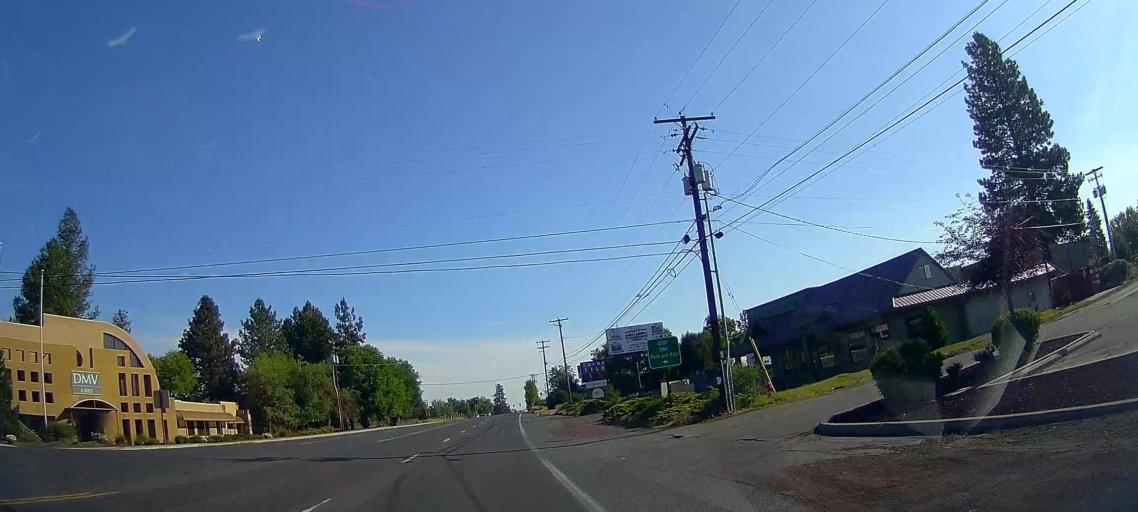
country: US
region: Oregon
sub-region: Deschutes County
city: Bend
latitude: 44.0879
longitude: -121.3060
